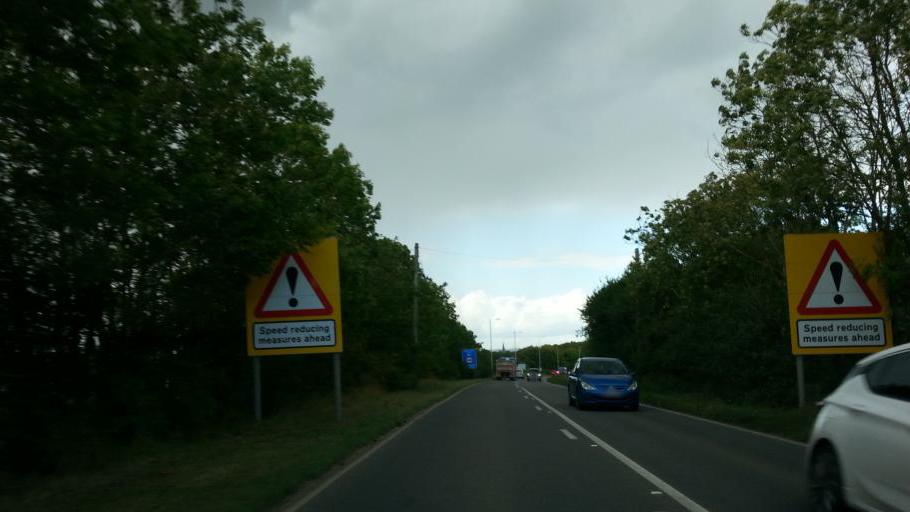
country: GB
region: England
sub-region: Cambridgeshire
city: Godmanchester
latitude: 52.3070
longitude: -0.1623
